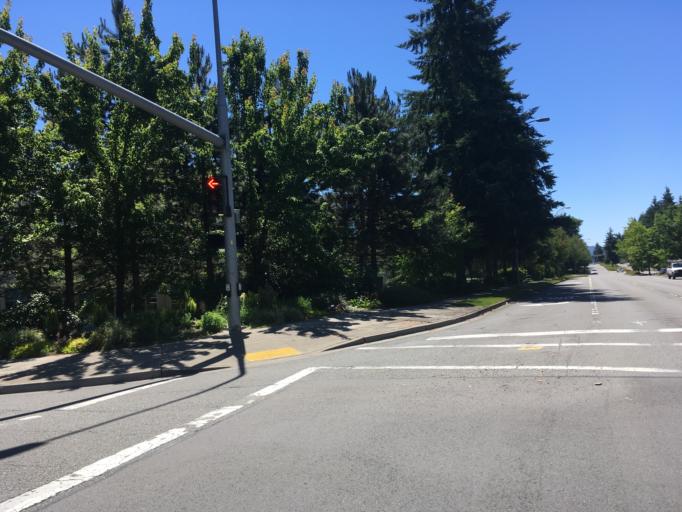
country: US
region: Washington
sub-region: King County
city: Redmond
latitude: 47.6459
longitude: -122.1428
